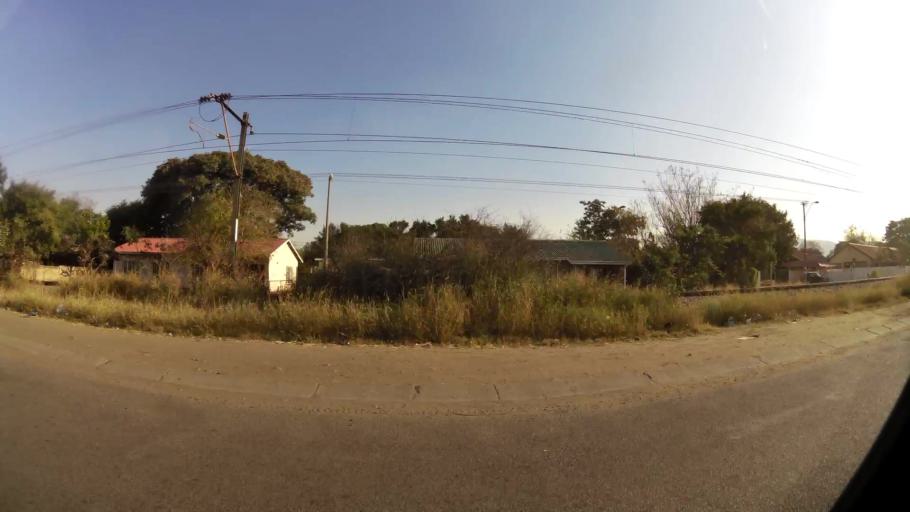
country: ZA
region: North-West
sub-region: Bojanala Platinum District Municipality
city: Rustenburg
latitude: -25.6502
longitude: 27.2385
